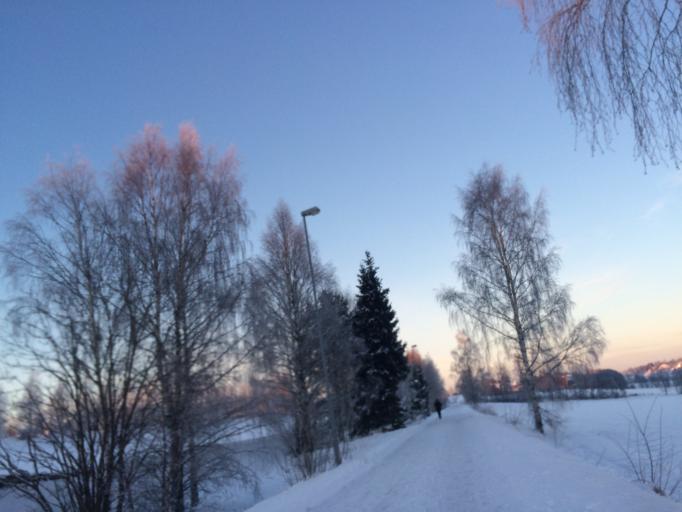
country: NO
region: Akershus
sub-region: Ski
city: Ski
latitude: 59.6982
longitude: 10.8327
